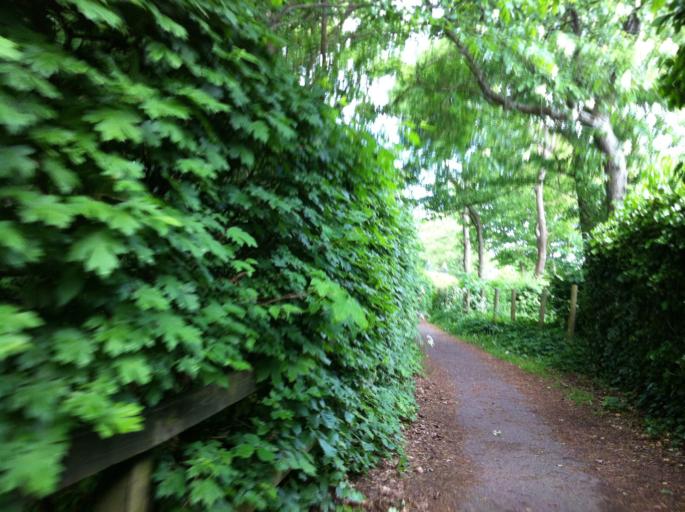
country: DK
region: Capital Region
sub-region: Gribskov Kommune
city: Gilleleje
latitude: 56.1270
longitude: 12.2943
